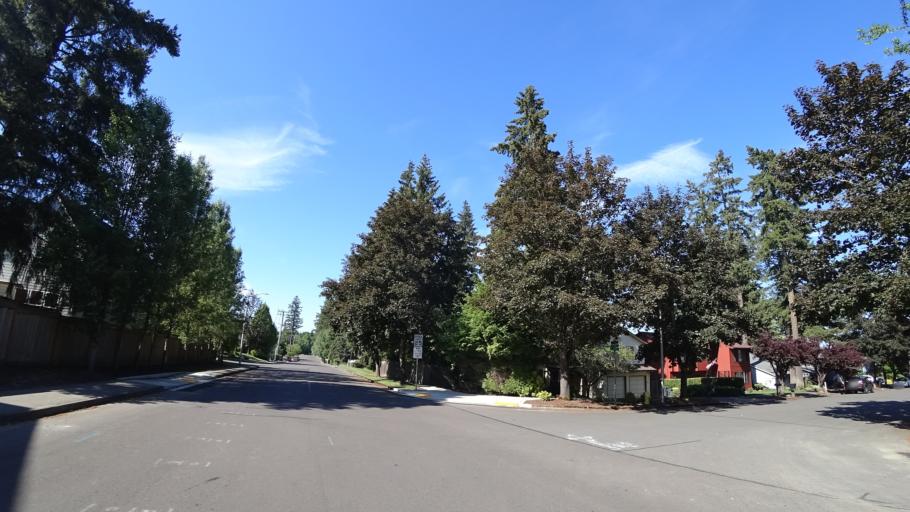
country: US
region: Oregon
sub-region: Washington County
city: Beaverton
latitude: 45.4516
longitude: -122.8106
